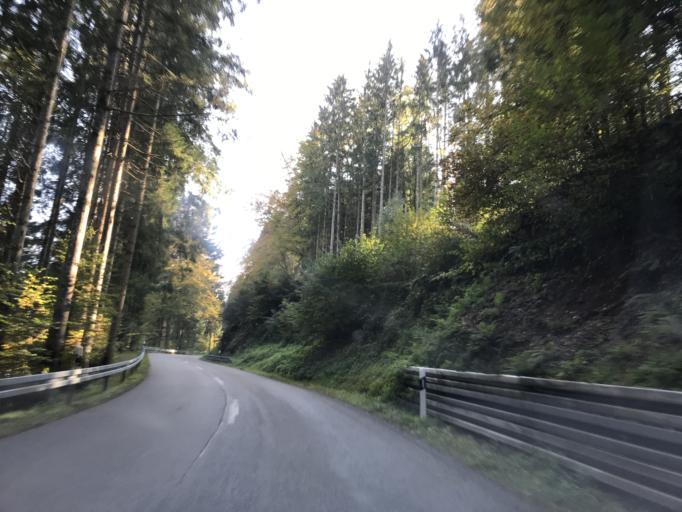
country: DE
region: Baden-Wuerttemberg
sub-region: Freiburg Region
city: Gorwihl
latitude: 47.6362
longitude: 8.0677
